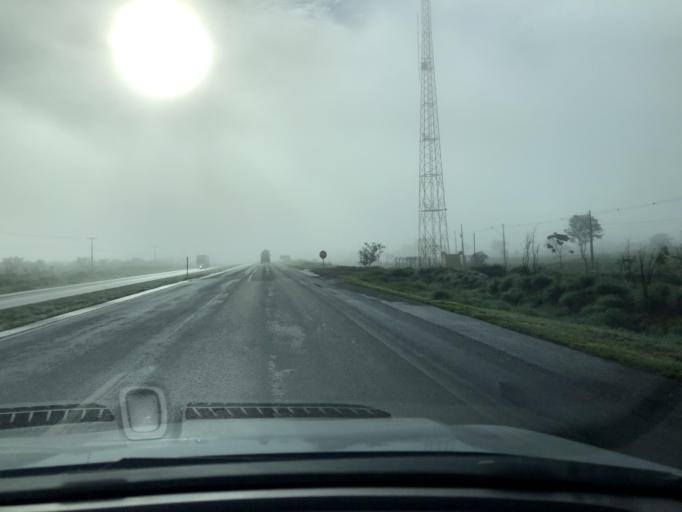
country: BR
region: Goias
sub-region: Luziania
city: Luziania
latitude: -16.2742
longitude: -47.8704
